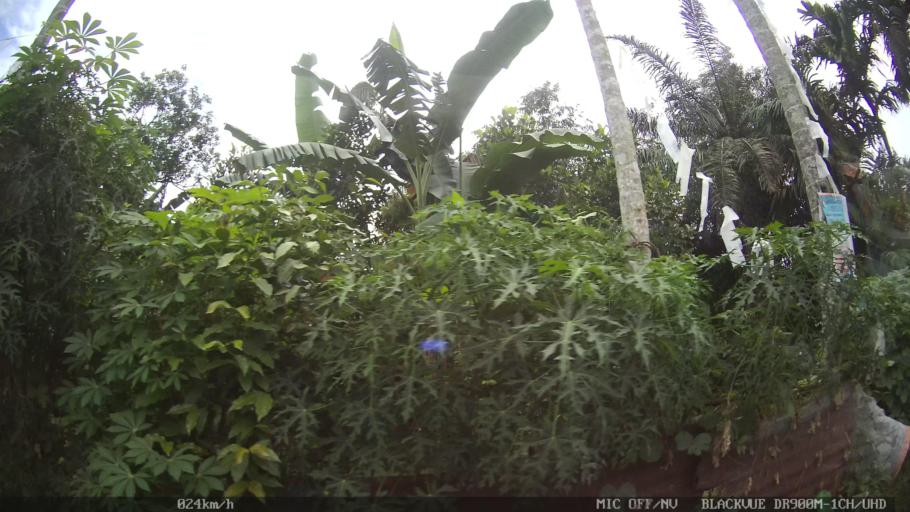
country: ID
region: North Sumatra
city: Sunggal
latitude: 3.6529
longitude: 98.5920
